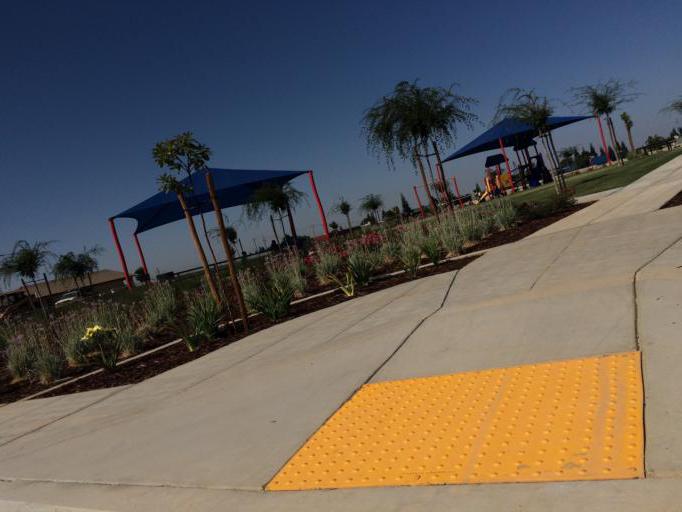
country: US
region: California
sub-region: Fresno County
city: Tarpey Village
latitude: 36.7740
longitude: -119.6799
